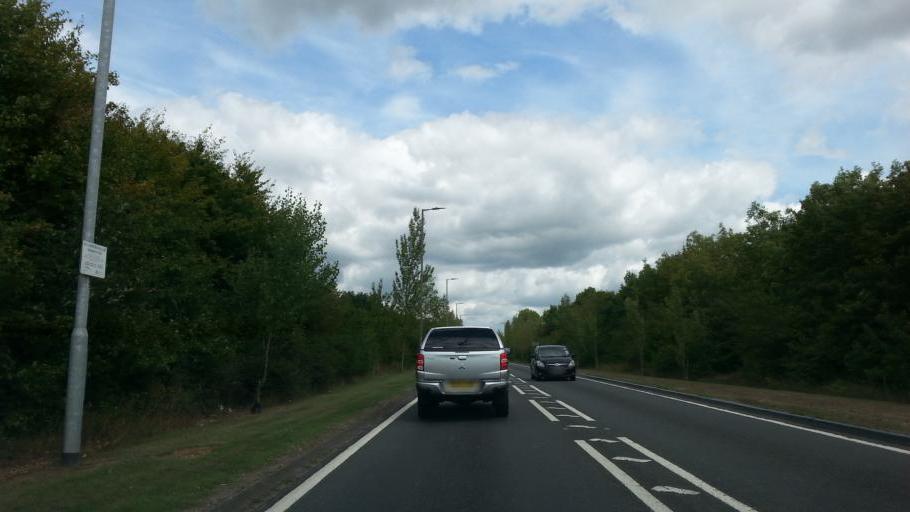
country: GB
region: England
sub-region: Essex
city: South Benfleet
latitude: 51.5593
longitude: 0.5402
